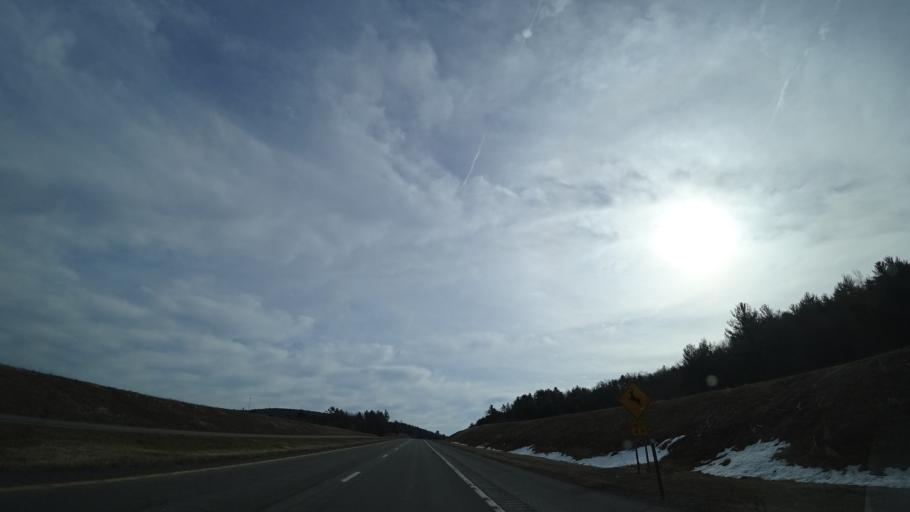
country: US
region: West Virginia
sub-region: Hardy County
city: Moorefield
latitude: 39.0457
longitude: -78.7269
